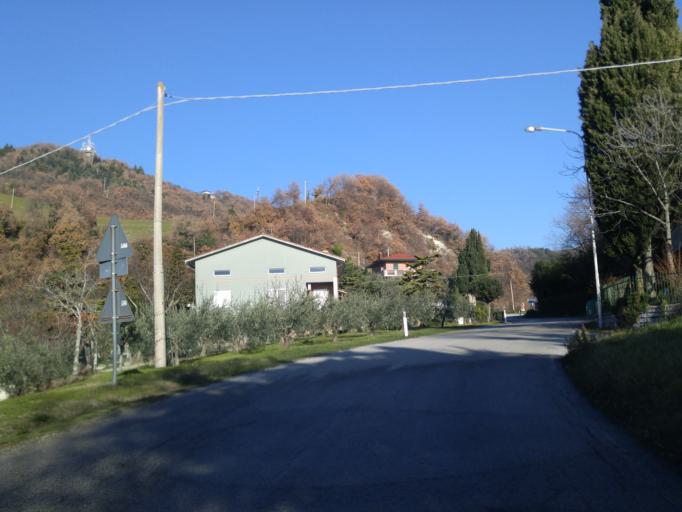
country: IT
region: The Marches
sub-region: Provincia di Pesaro e Urbino
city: Isola del Piano
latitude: 43.7657
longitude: 12.8005
